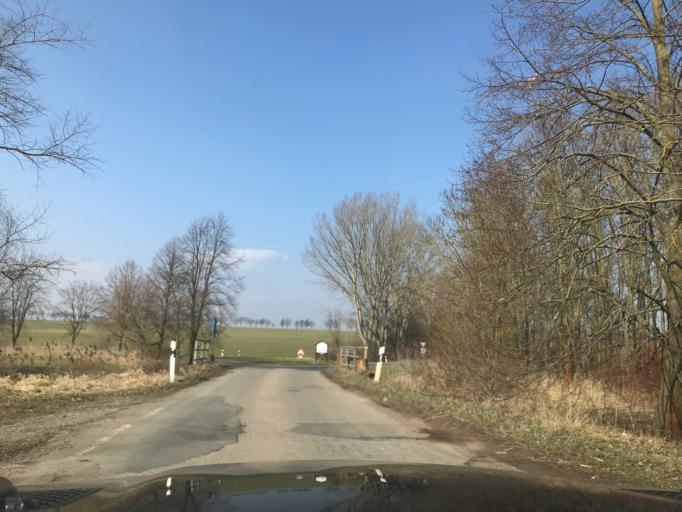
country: DE
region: Thuringia
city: Heroldishausen
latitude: 51.1394
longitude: 10.5250
